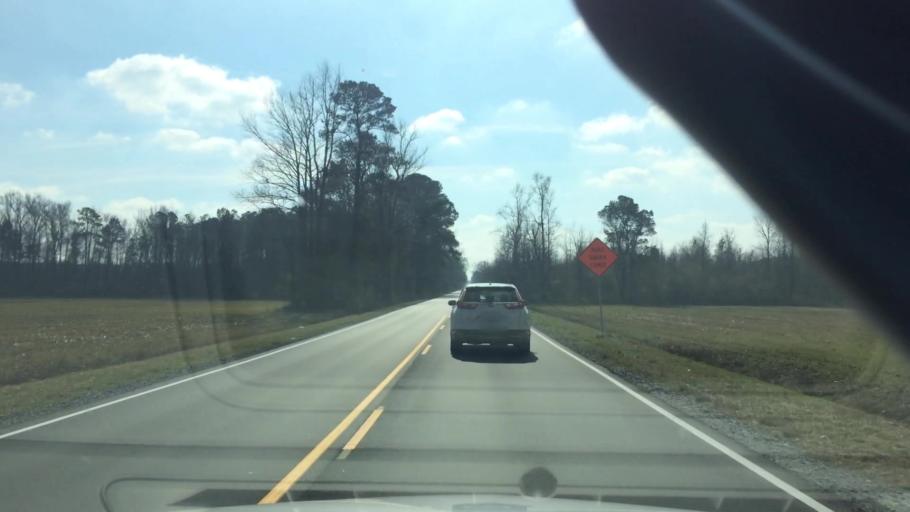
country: US
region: North Carolina
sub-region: Duplin County
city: Beulaville
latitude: 34.9535
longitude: -77.7664
